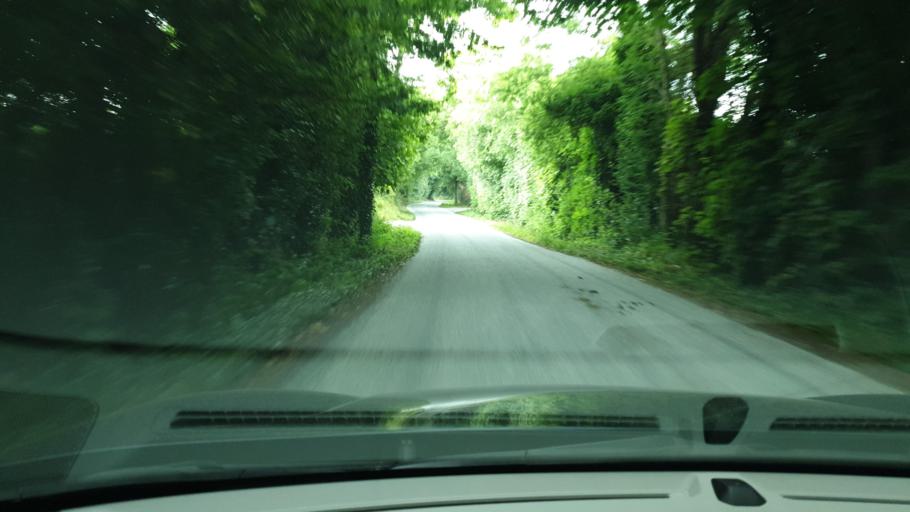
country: IE
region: Leinster
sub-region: An Mhi
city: Dunshaughlin
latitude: 53.4949
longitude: -6.5100
